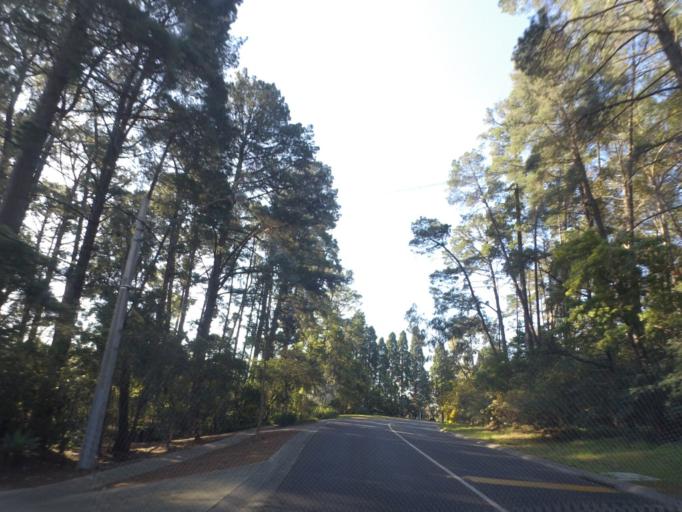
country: AU
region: Victoria
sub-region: Manningham
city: Donvale
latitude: -37.7897
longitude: 145.1756
